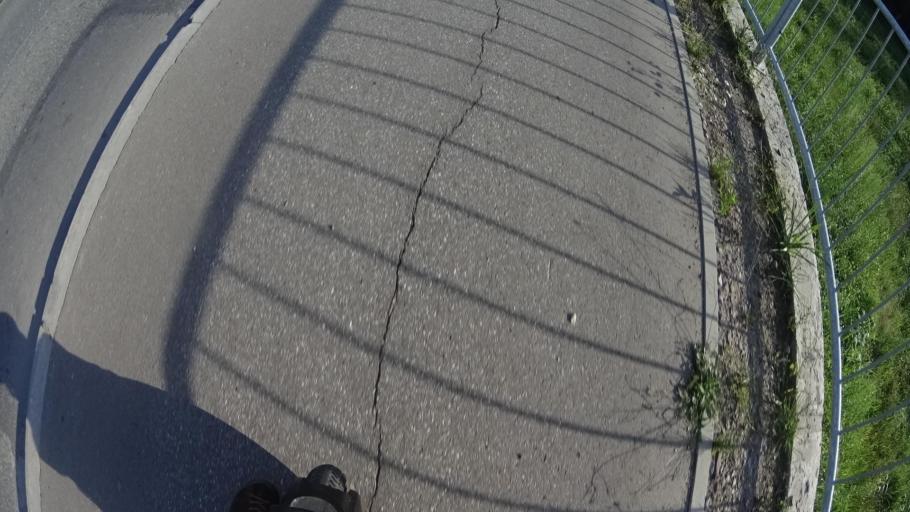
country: PL
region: Masovian Voivodeship
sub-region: Powiat pruszkowski
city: Nadarzyn
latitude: 52.0338
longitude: 20.7825
